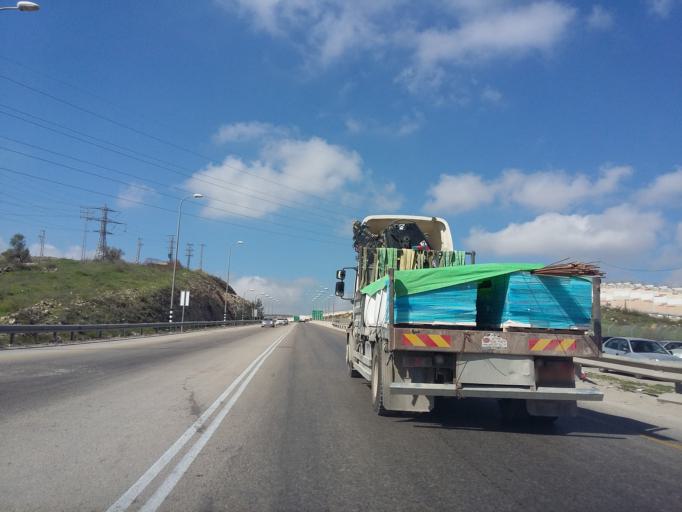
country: PS
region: West Bank
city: Qalandiya
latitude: 31.8600
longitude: 35.2145
